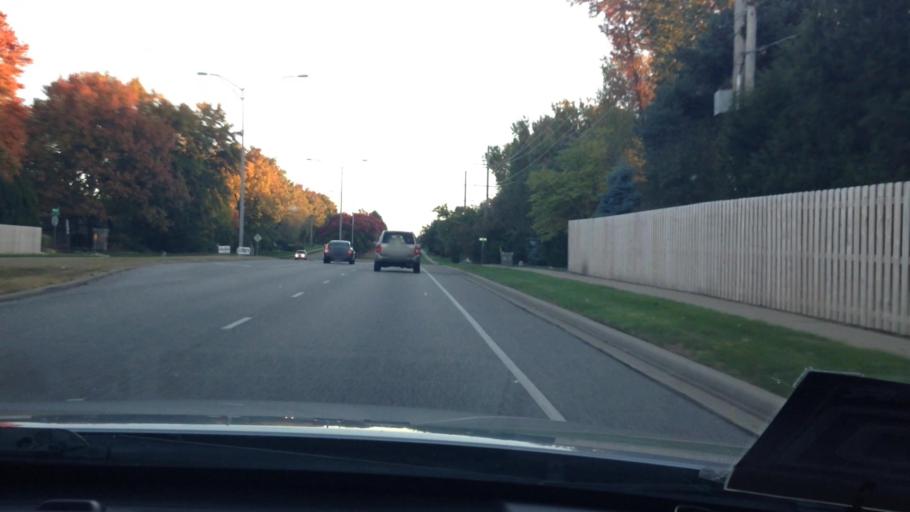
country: US
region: Kansas
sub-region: Johnson County
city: Lenexa
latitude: 38.9106
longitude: -94.7053
